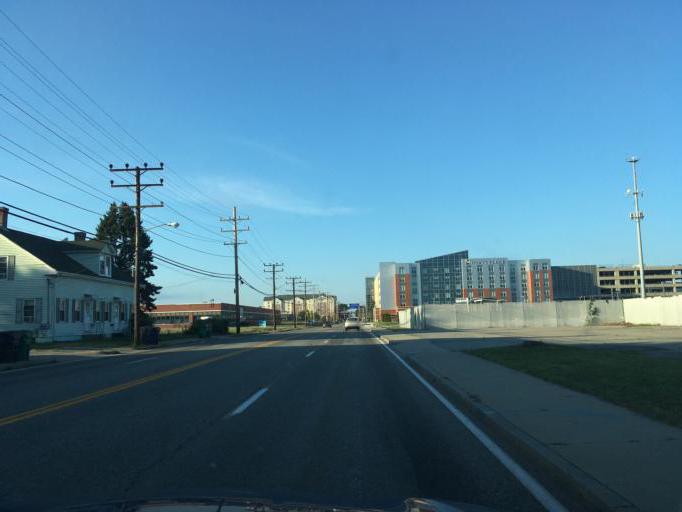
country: US
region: Rhode Island
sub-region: Kent County
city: Warwick
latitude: 41.7246
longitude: -71.4445
